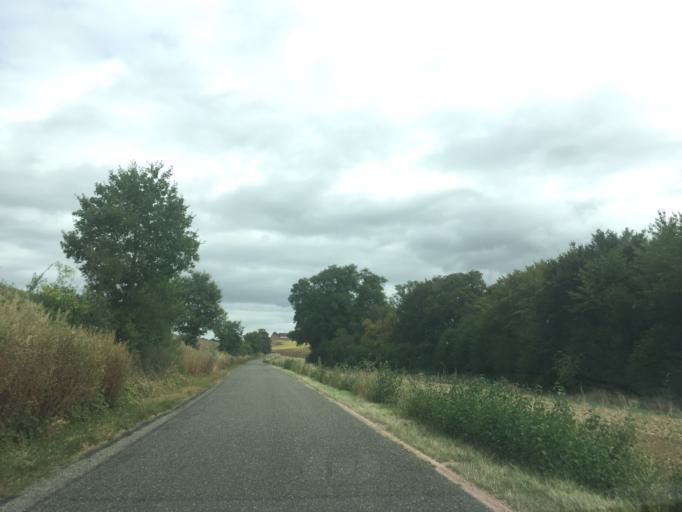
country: FR
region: Midi-Pyrenees
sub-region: Departement du Gers
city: Vic-Fezensac
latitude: 43.6667
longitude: 0.3569
